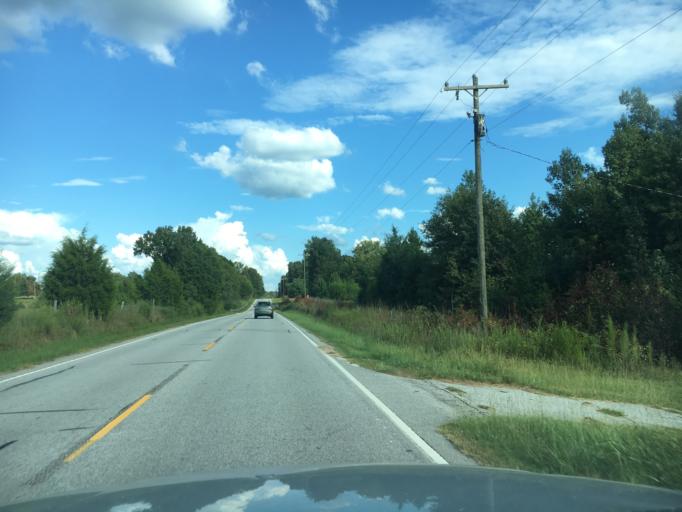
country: US
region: South Carolina
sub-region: Greenwood County
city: Ware Shoals
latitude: 34.5220
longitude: -82.1748
